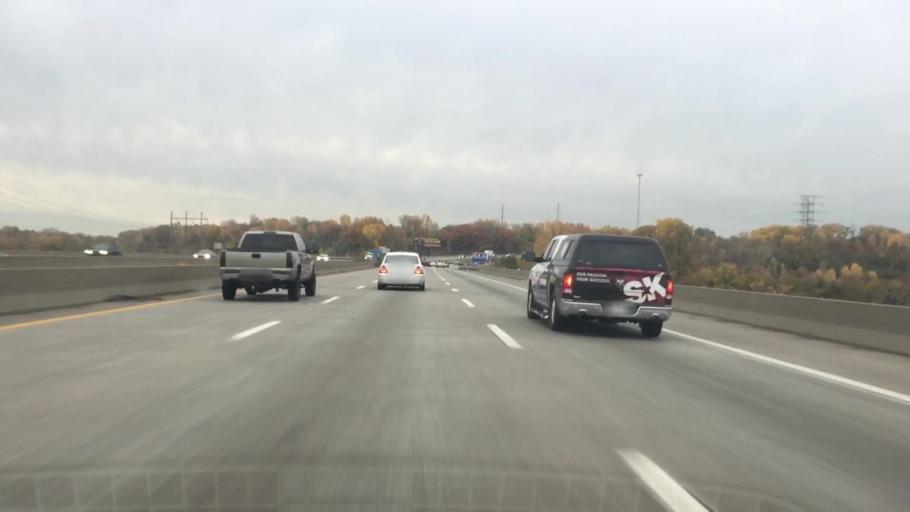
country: US
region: Missouri
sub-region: Jackson County
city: Sugar Creek
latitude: 39.1185
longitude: -94.4896
